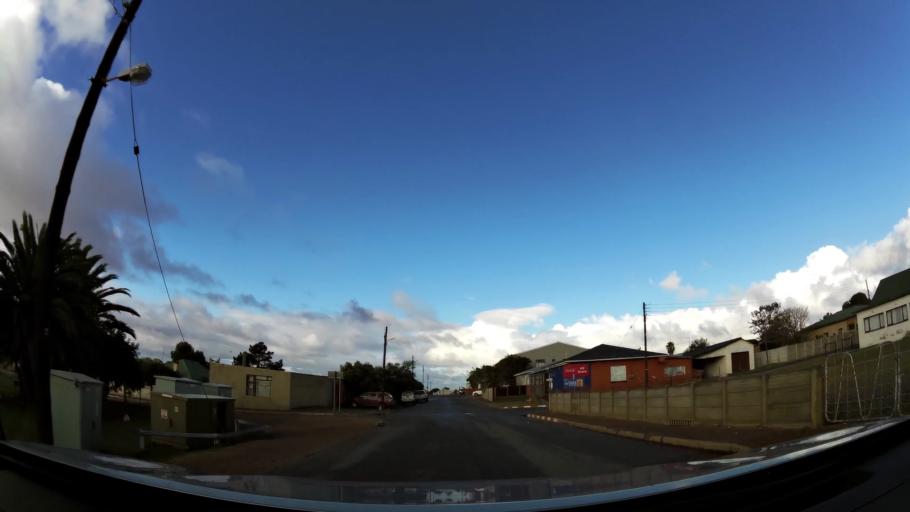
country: ZA
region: Western Cape
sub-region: Eden District Municipality
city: Riversdale
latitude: -34.2033
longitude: 21.5810
